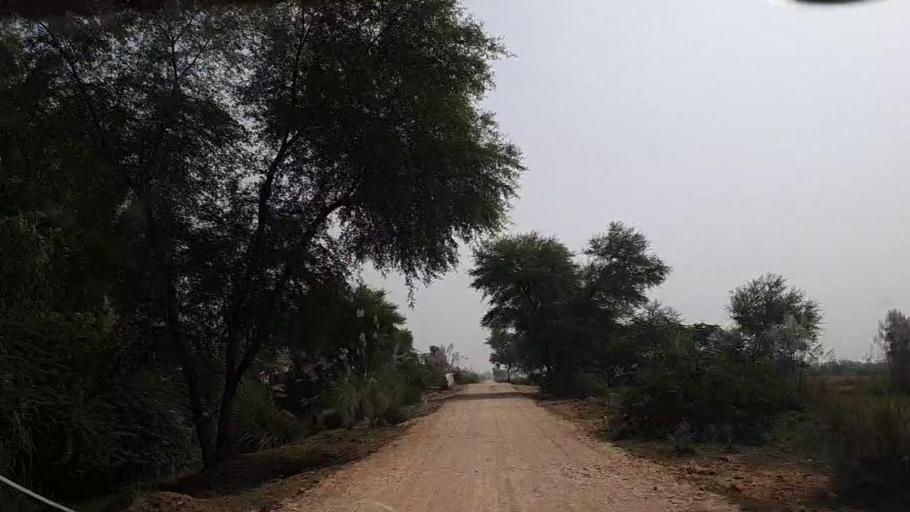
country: PK
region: Sindh
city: Garhi Yasin
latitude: 27.9302
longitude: 68.5586
